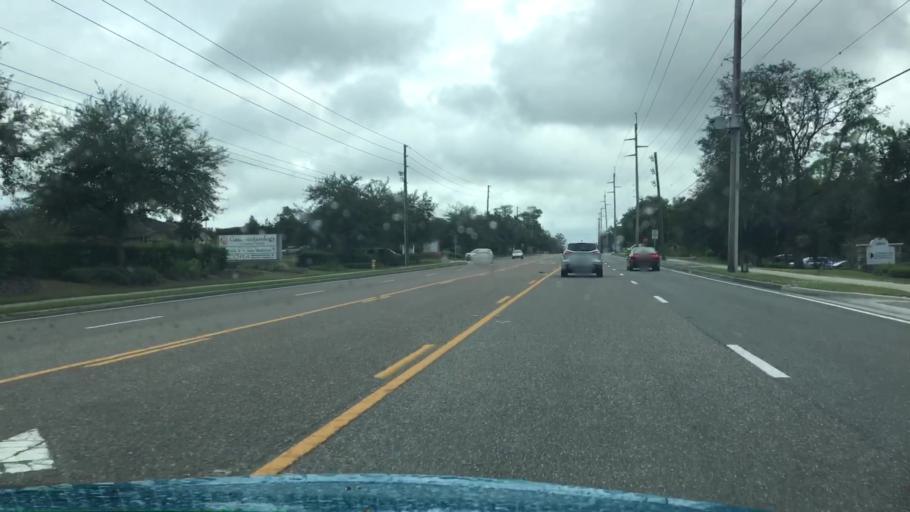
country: US
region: Florida
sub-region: Volusia County
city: Deltona
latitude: 28.8991
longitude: -81.2856
